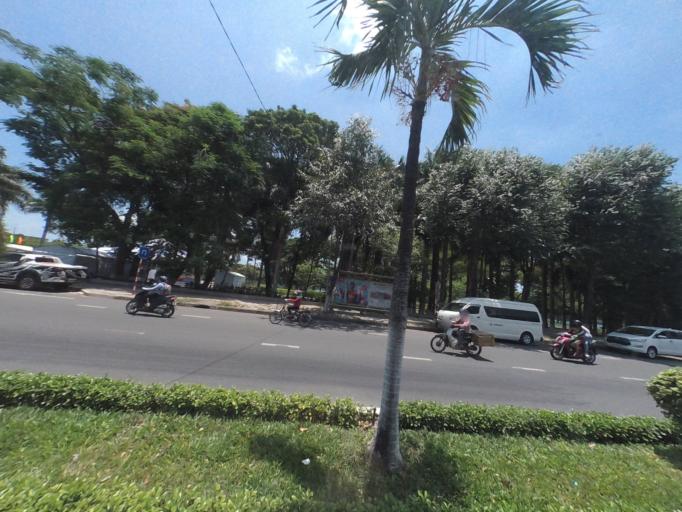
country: VN
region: Da Nang
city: Thanh Khe
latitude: 16.0622
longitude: 108.2043
